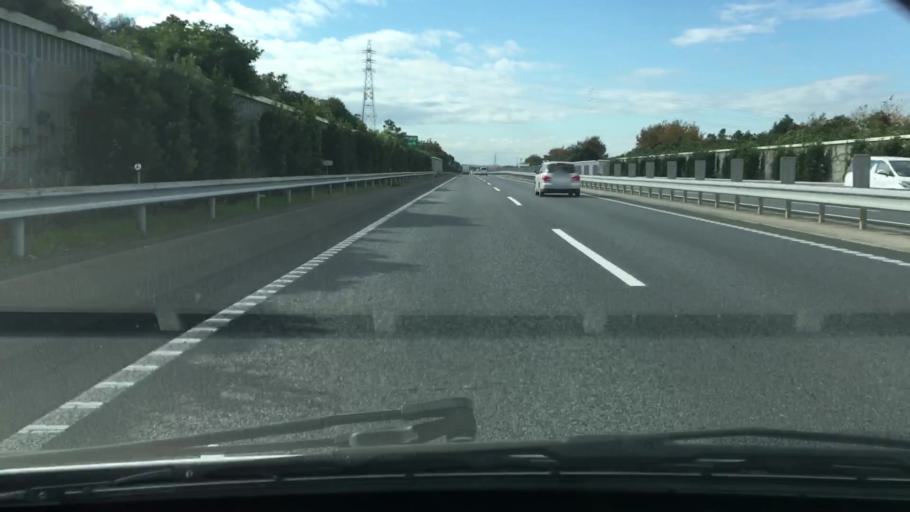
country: JP
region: Chiba
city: Ichihara
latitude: 35.5251
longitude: 140.1266
